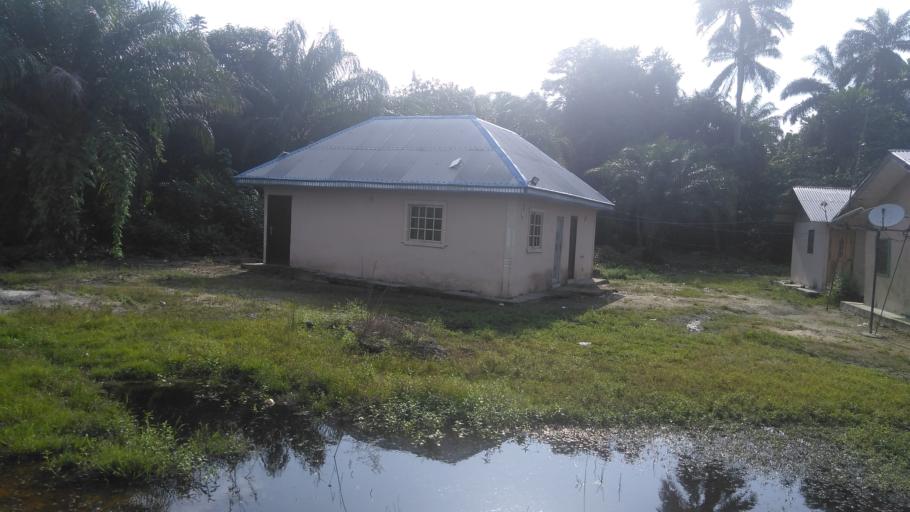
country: NG
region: Delta
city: Sapele
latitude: 5.8409
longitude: 5.1272
